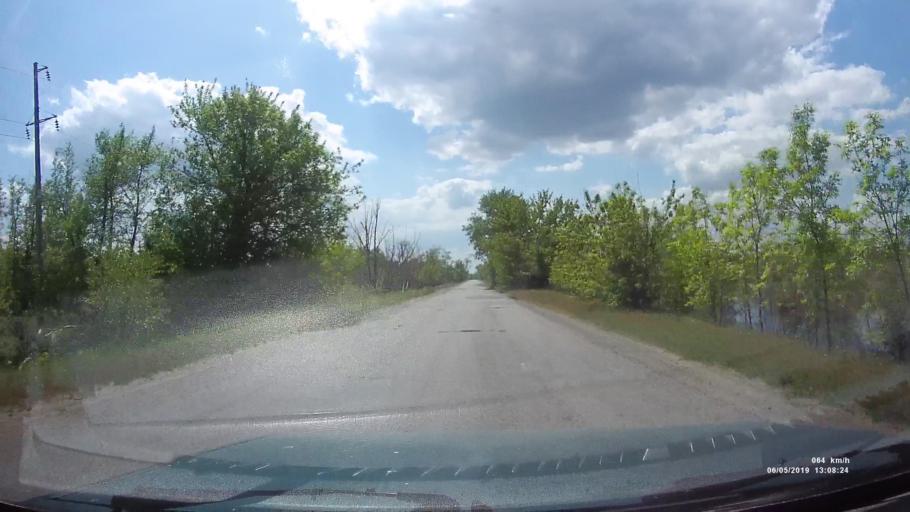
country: RU
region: Rostov
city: Ust'-Donetskiy
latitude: 47.7759
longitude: 40.9958
